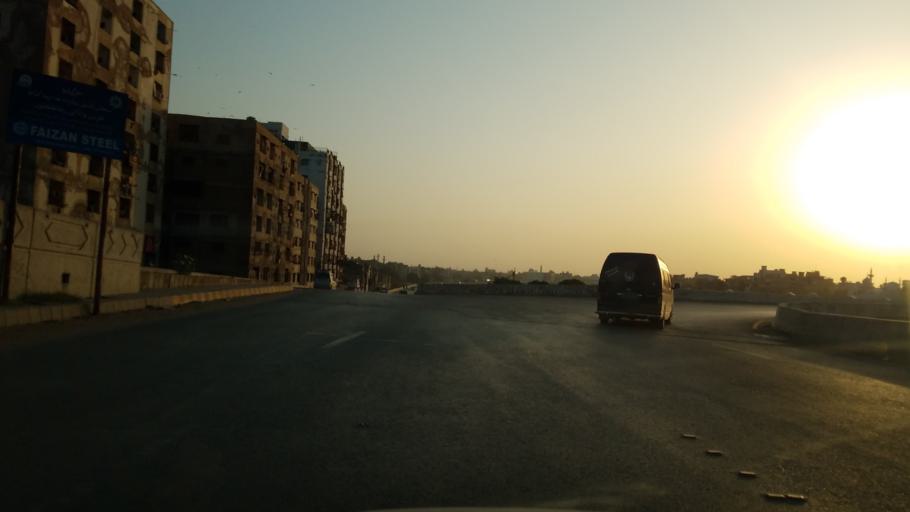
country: PK
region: Sindh
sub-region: Karachi District
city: Karachi
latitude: 24.8821
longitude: 67.0203
